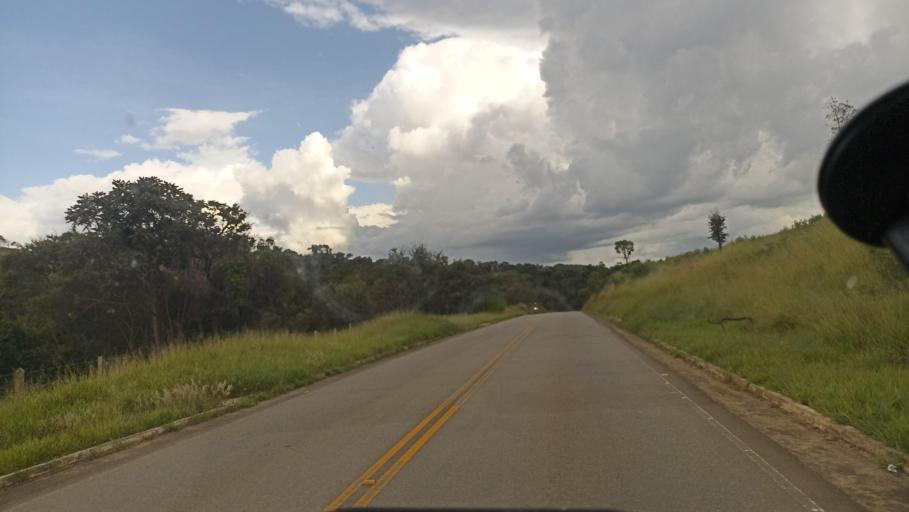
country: BR
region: Minas Gerais
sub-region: Cruzilia
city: Cruzilia
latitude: -21.8998
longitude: -44.8192
